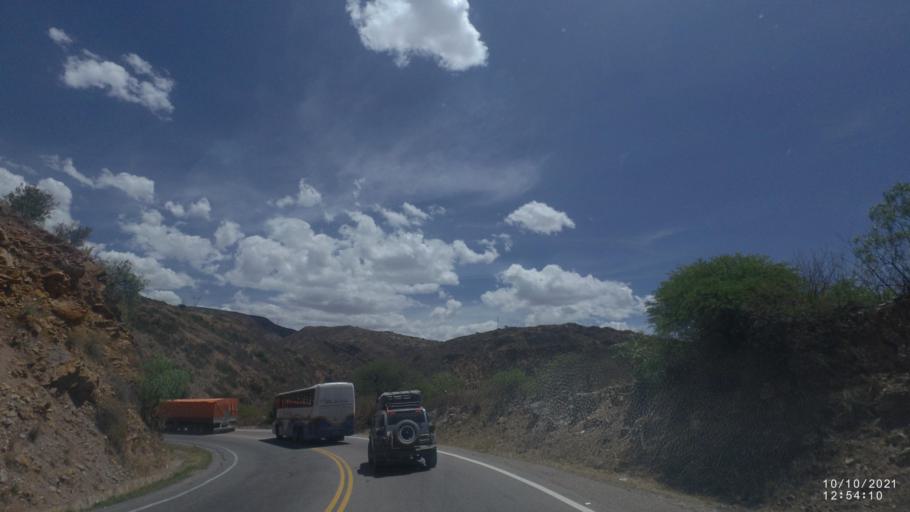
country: BO
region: Cochabamba
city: Capinota
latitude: -17.6112
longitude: -66.3583
